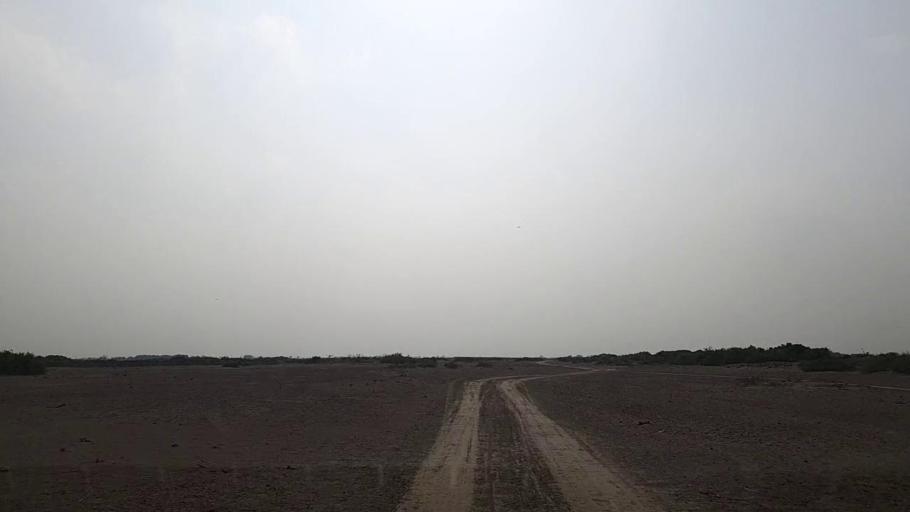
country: PK
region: Sindh
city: Gharo
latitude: 24.6717
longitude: 67.6420
